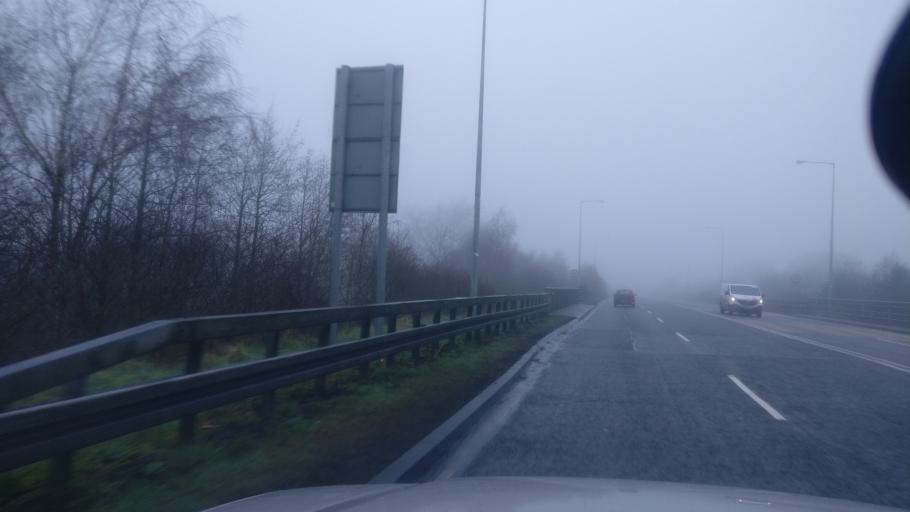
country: IE
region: Munster
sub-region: County Limerick
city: Annacotty
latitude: 52.6479
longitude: -8.5664
